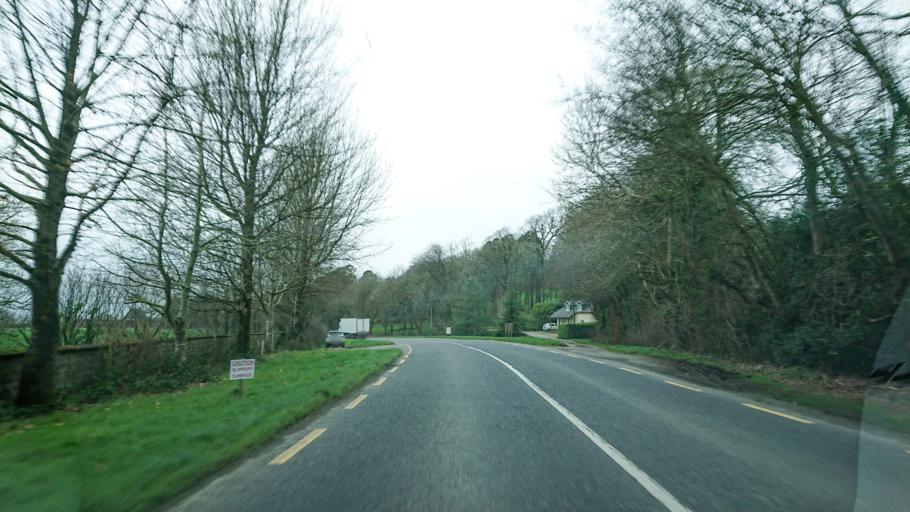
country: IE
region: Munster
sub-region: County Cork
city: Bandon
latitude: 51.7464
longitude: -8.7875
